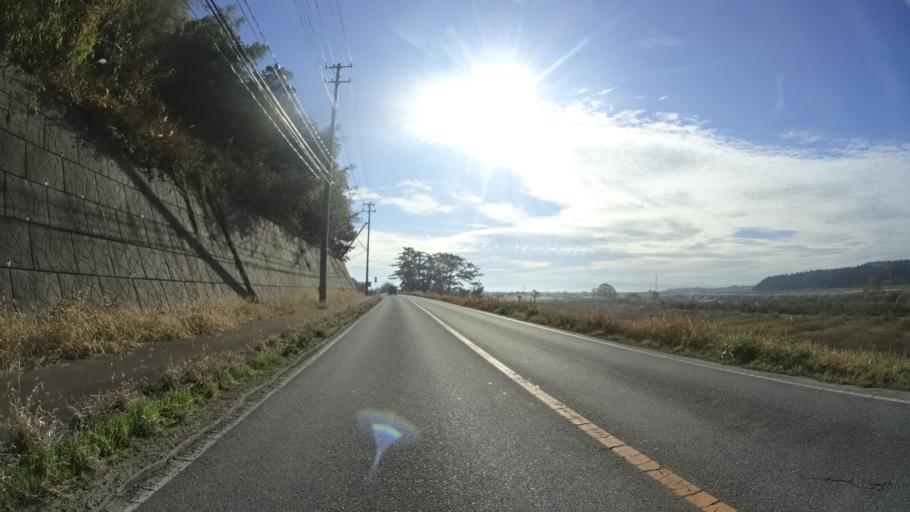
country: JP
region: Niigata
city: Yoshida-kasugacho
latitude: 37.6514
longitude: 138.8115
